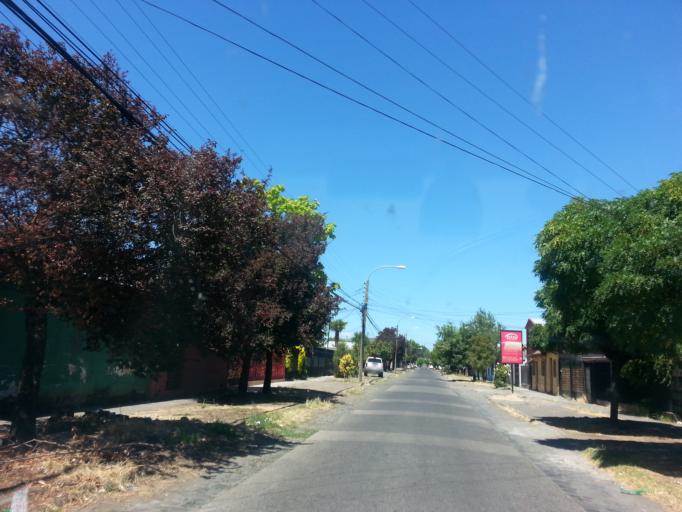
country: CL
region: Biobio
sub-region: Provincia de Nuble
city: Chillan
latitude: -36.6065
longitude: -72.0903
